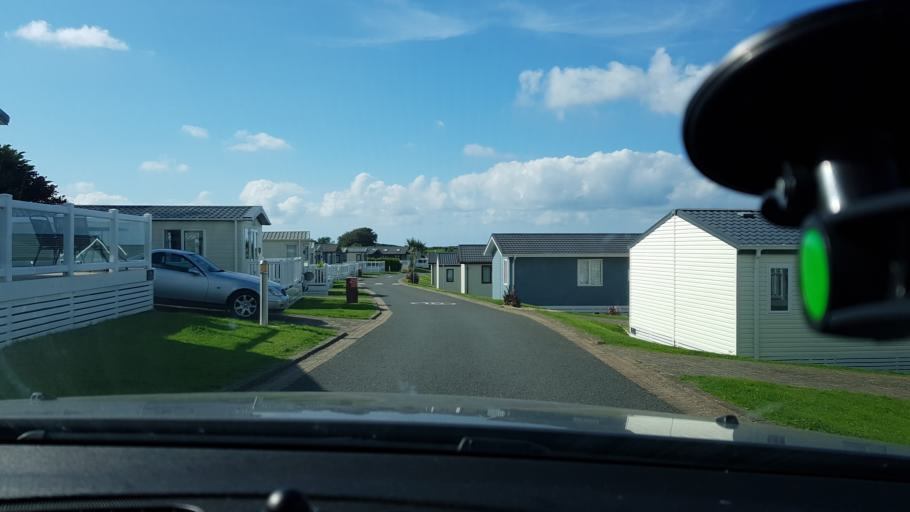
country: GB
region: England
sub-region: Cornwall
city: Tintagel
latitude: 50.6682
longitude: -4.7396
